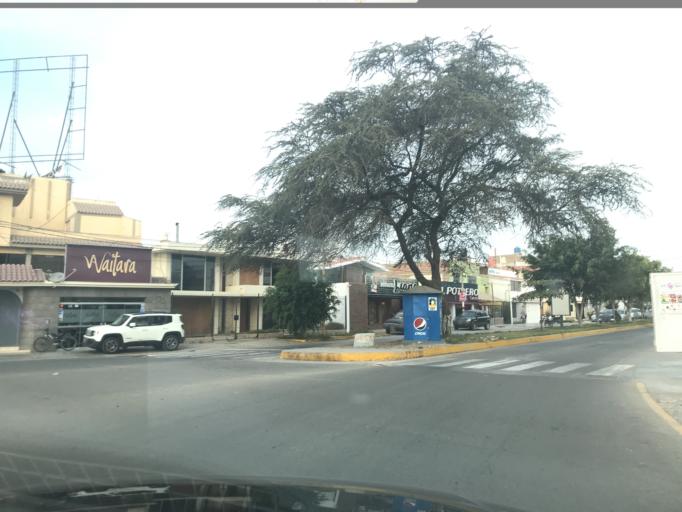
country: PE
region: Lambayeque
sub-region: Provincia de Chiclayo
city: Chiclayo
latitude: -6.7822
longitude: -79.8426
